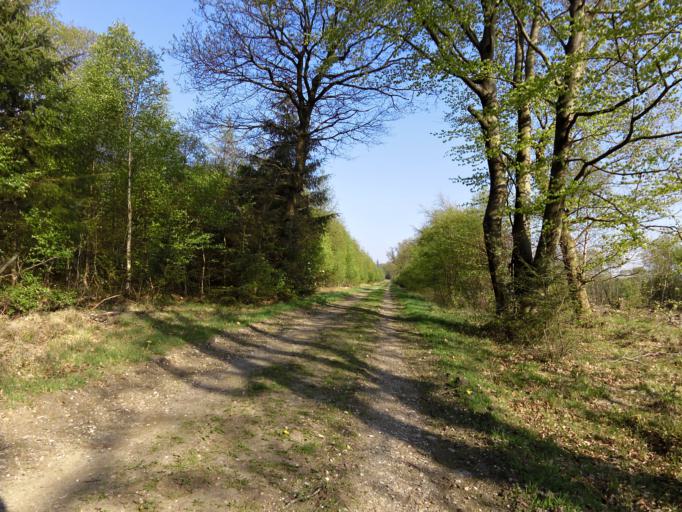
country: DK
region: South Denmark
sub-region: Tonder Kommune
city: Toftlund
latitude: 55.1957
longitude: 8.9408
